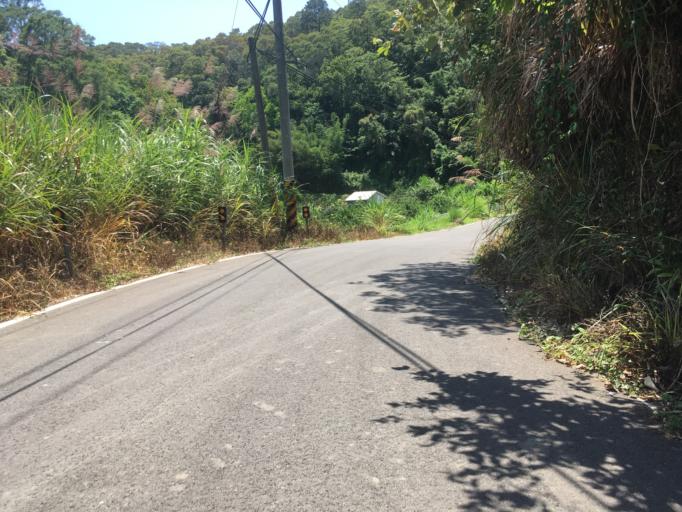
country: TW
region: Taiwan
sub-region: Hsinchu
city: Hsinchu
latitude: 24.7302
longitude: 120.9837
